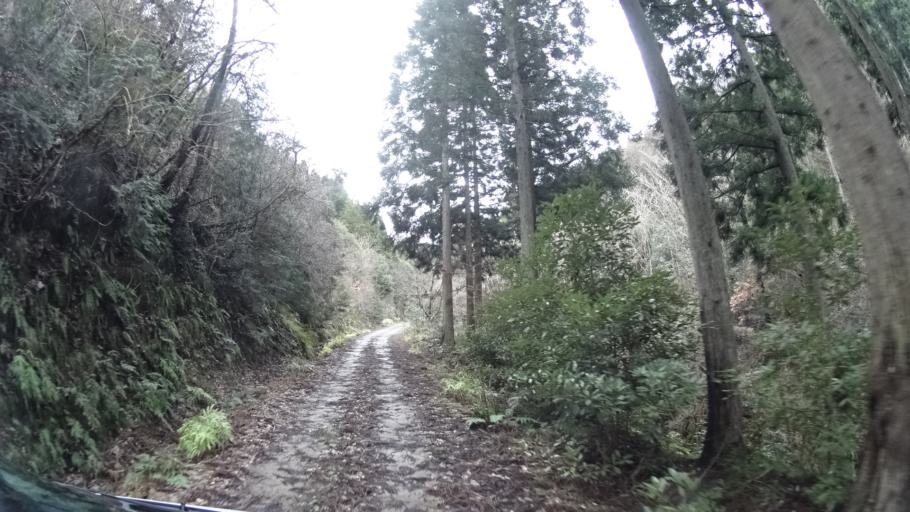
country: JP
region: Kyoto
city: Ayabe
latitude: 35.3122
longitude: 135.3737
